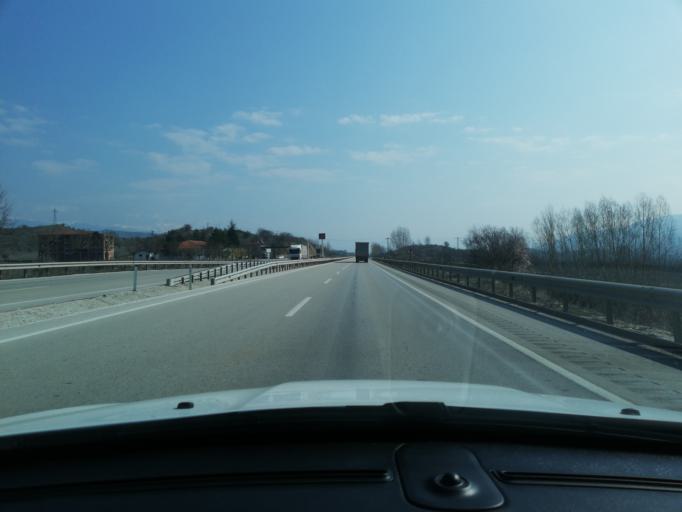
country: TR
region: Cankiri
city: Beloren
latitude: 40.8683
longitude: 33.4894
